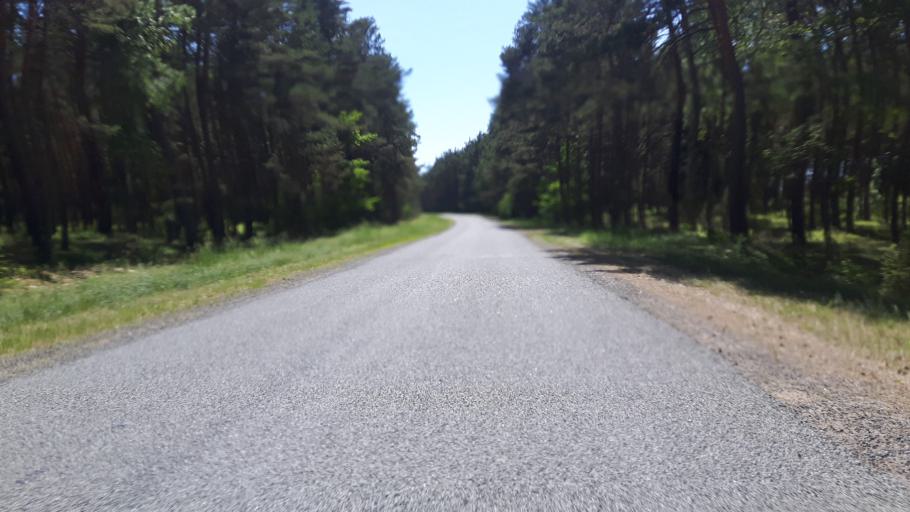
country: LV
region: Salacgrivas
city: Ainazi
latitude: 57.9711
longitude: 24.4099
